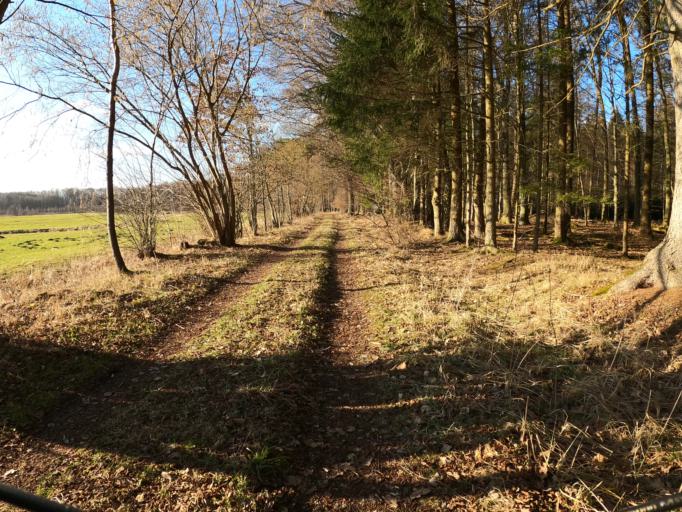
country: DE
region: Bavaria
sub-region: Swabia
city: Bubesheim
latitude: 48.4184
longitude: 10.2256
